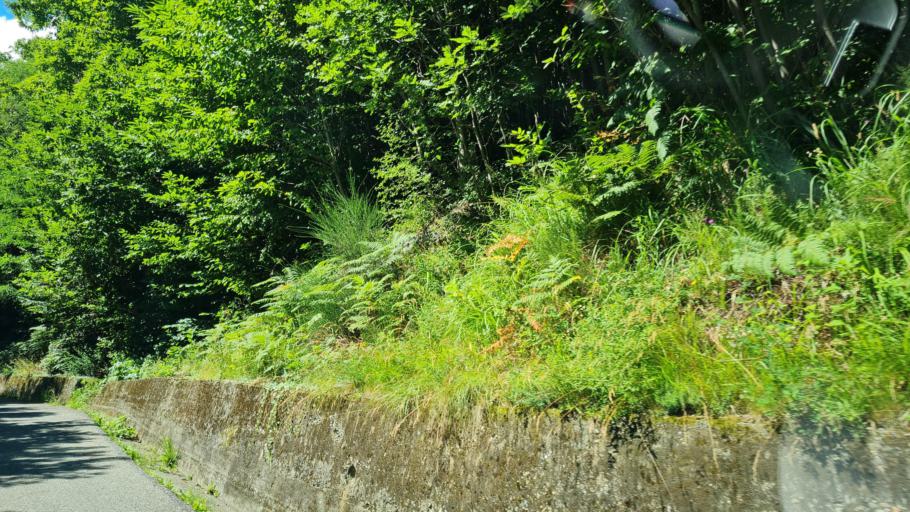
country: IT
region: Piedmont
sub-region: Provincia di Torino
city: Quincinetto
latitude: 45.5563
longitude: 7.8045
